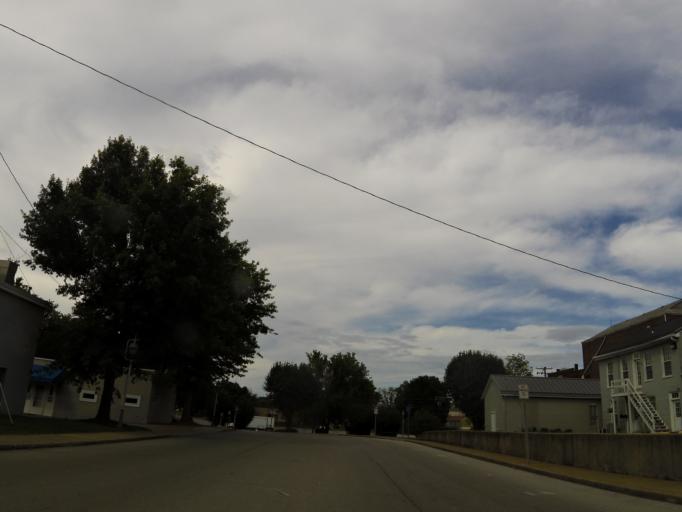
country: US
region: Kentucky
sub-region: Christian County
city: Hopkinsville
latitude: 36.8671
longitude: -87.4891
